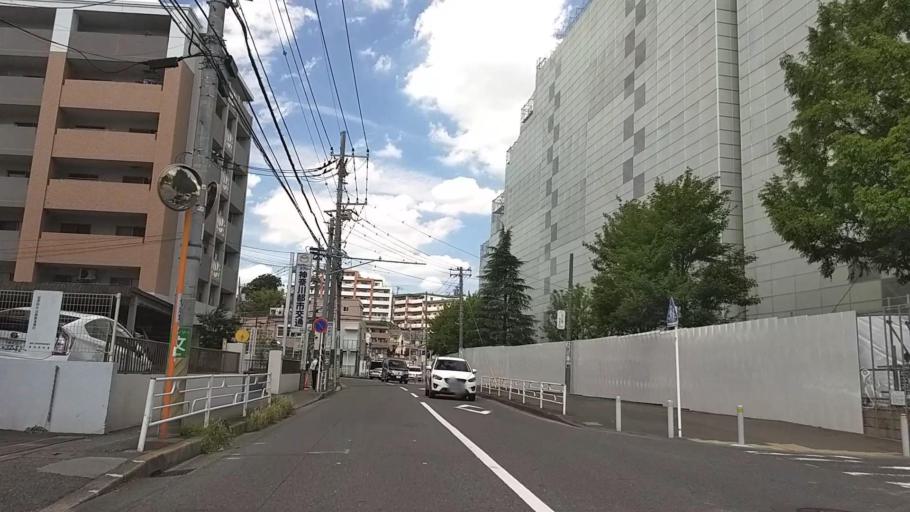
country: JP
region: Kanagawa
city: Yokohama
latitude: 35.5174
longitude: 139.5634
